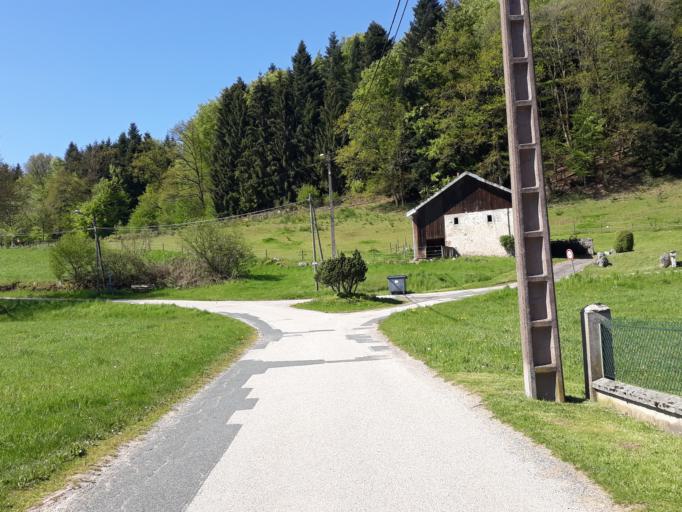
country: FR
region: Lorraine
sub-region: Departement des Vosges
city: Granges-sur-Vologne
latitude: 48.1373
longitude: 6.7915
